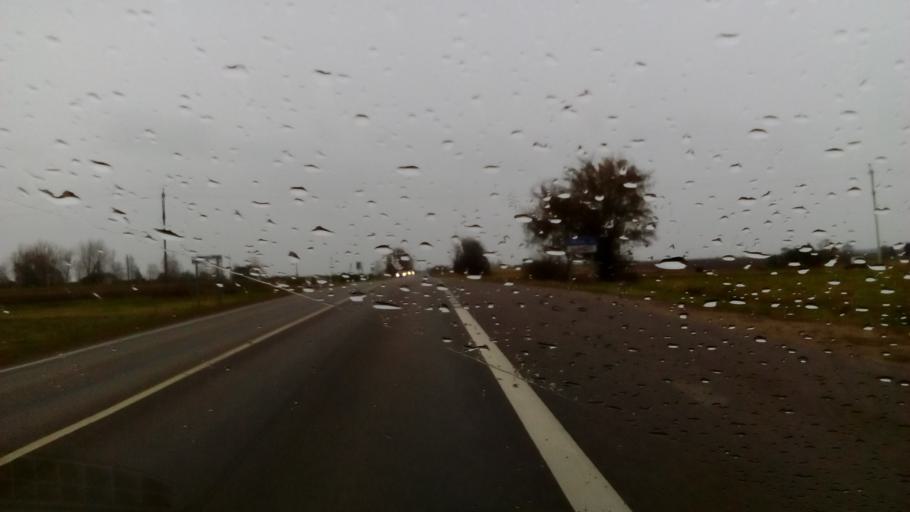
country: LT
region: Marijampoles apskritis
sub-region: Marijampole Municipality
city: Marijampole
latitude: 54.5638
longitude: 23.5400
